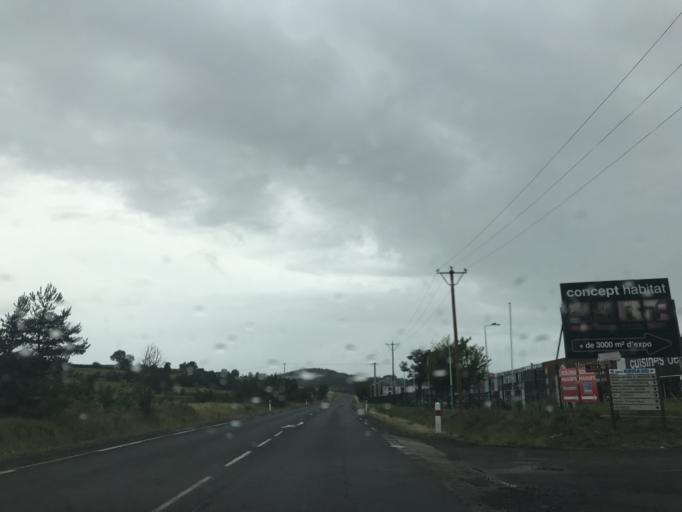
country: FR
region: Auvergne
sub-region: Departement de la Haute-Loire
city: Polignac
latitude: 45.0787
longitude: 3.8340
